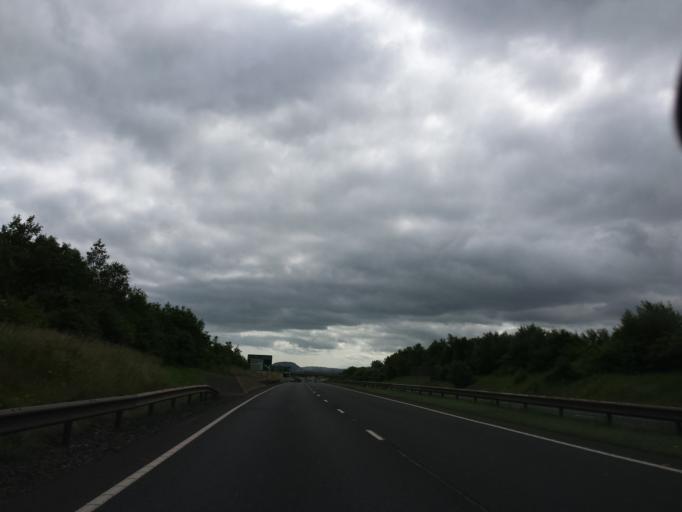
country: GB
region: Scotland
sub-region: East Lothian
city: Longniddry
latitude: 55.9539
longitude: -2.8444
